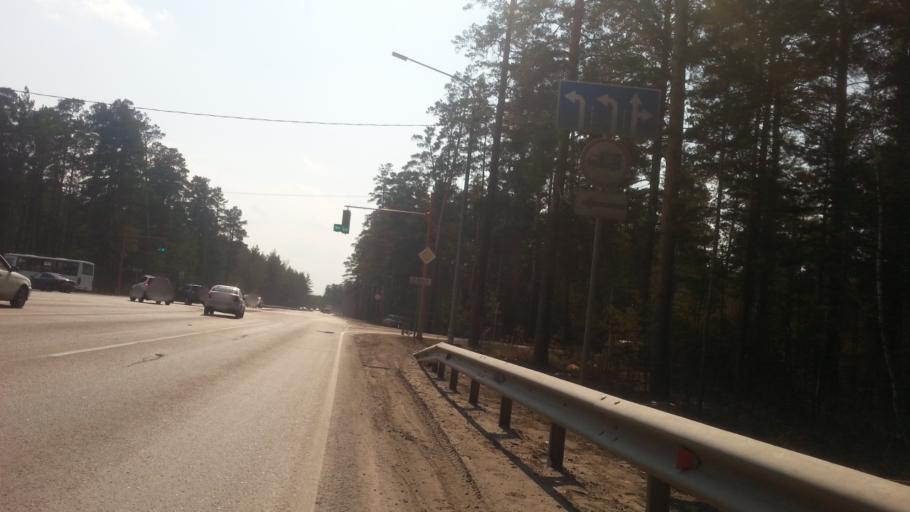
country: RU
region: Altai Krai
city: Yuzhnyy
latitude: 53.3151
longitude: 83.7040
